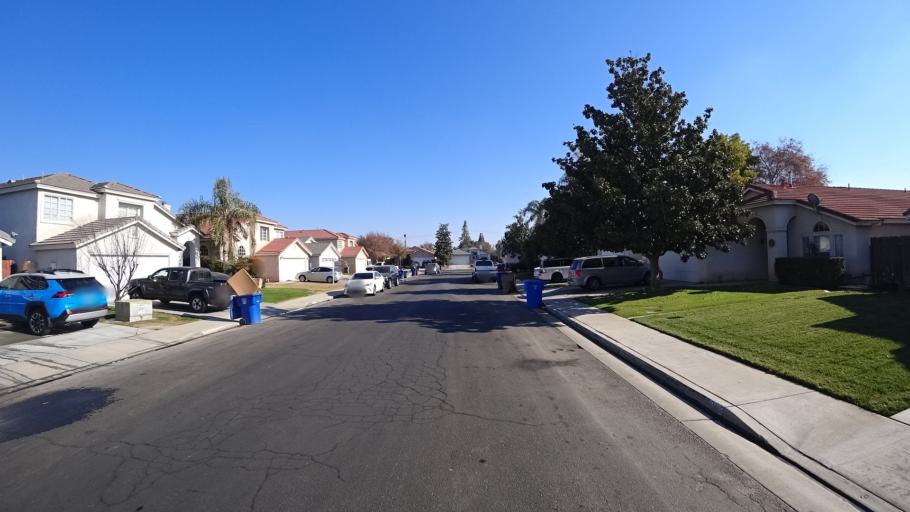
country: US
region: California
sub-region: Kern County
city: Greenfield
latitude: 35.2996
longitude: -119.0582
